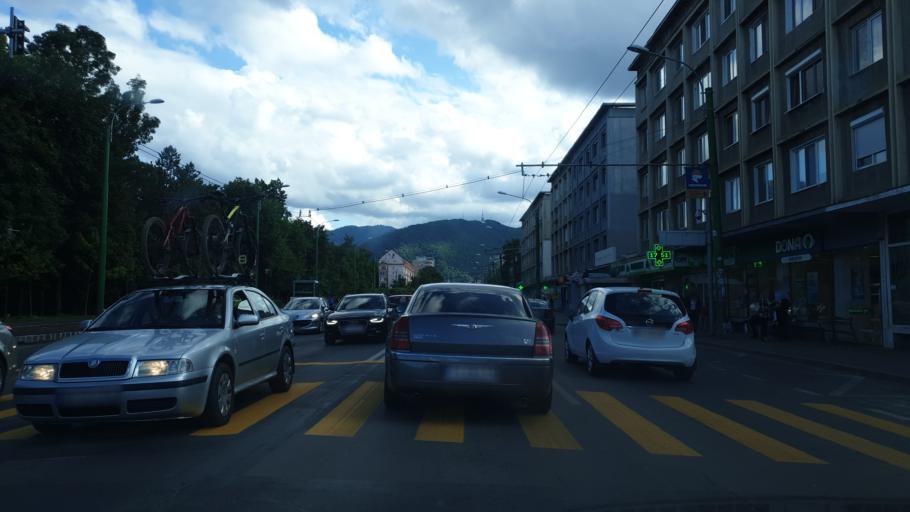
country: RO
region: Brasov
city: Brasov
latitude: 45.6650
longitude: 25.6091
